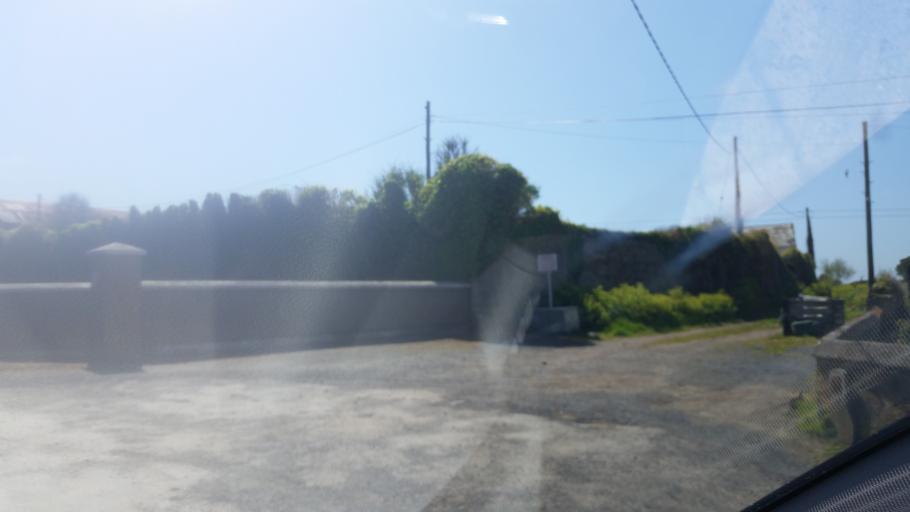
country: IE
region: Munster
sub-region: Waterford
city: Dunmore East
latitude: 52.1340
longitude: -6.9108
